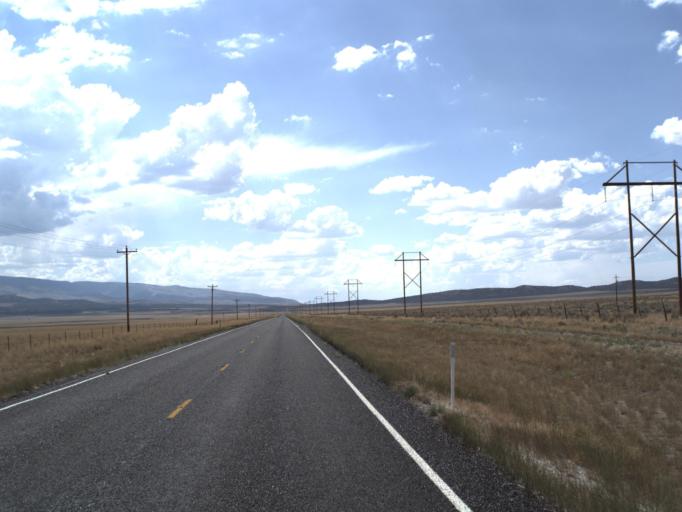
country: US
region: Idaho
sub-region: Oneida County
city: Malad City
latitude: 41.9656
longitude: -113.0621
